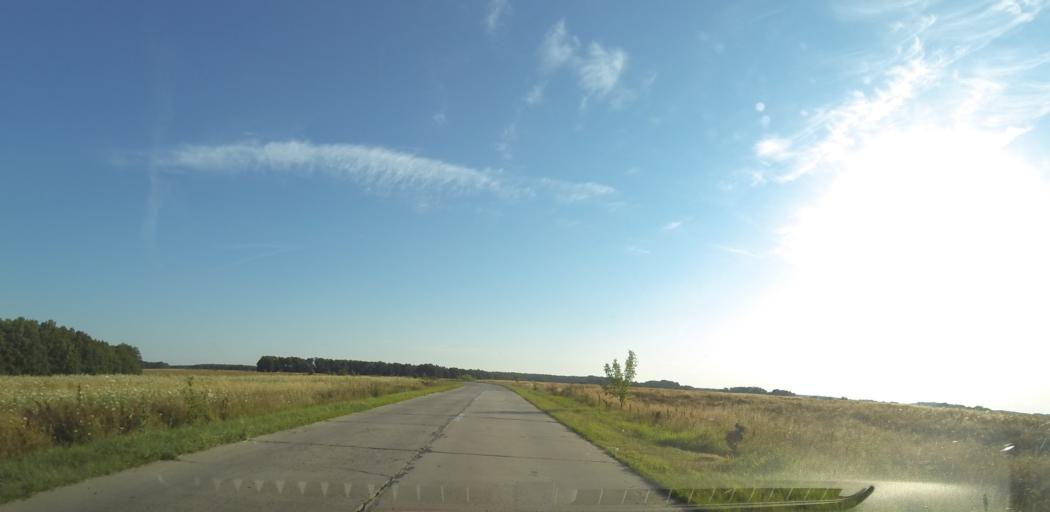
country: RO
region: Dolj
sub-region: Comuna Bulzesti
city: Bulzesti
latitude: 44.5528
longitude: 23.9075
